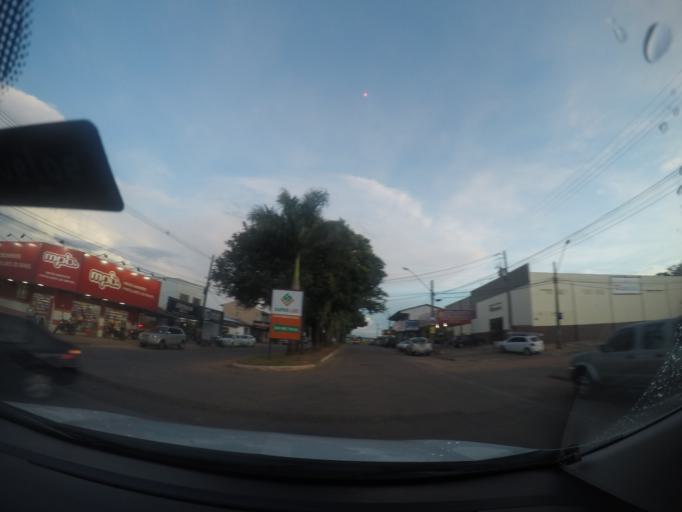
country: BR
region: Goias
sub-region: Goiania
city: Goiania
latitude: -16.7239
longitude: -49.3729
